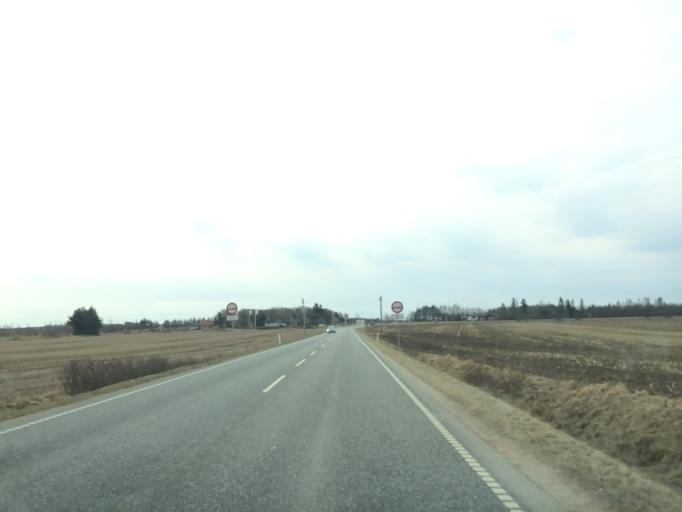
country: DK
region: Central Jutland
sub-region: Ringkobing-Skjern Kommune
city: Videbaek
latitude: 56.0901
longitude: 8.5074
